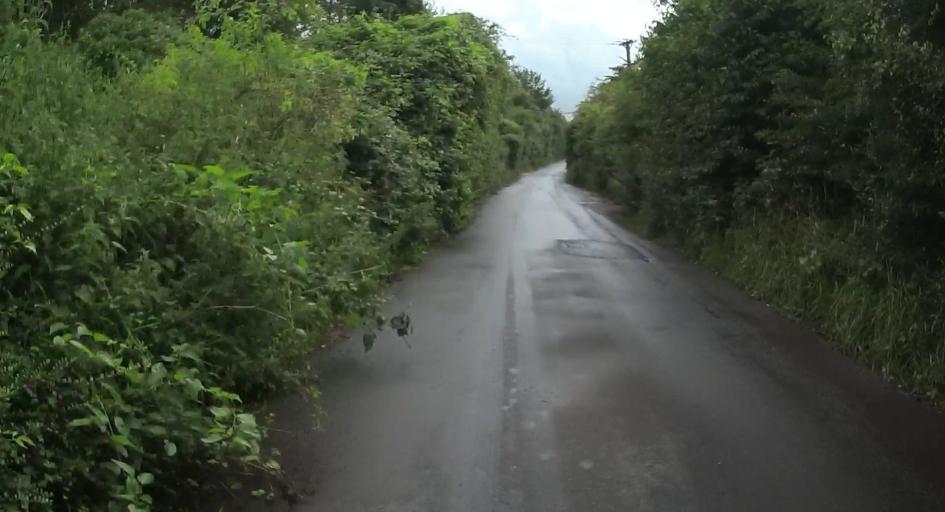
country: GB
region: England
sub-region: Hampshire
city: Andover
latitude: 51.2214
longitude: -1.4335
